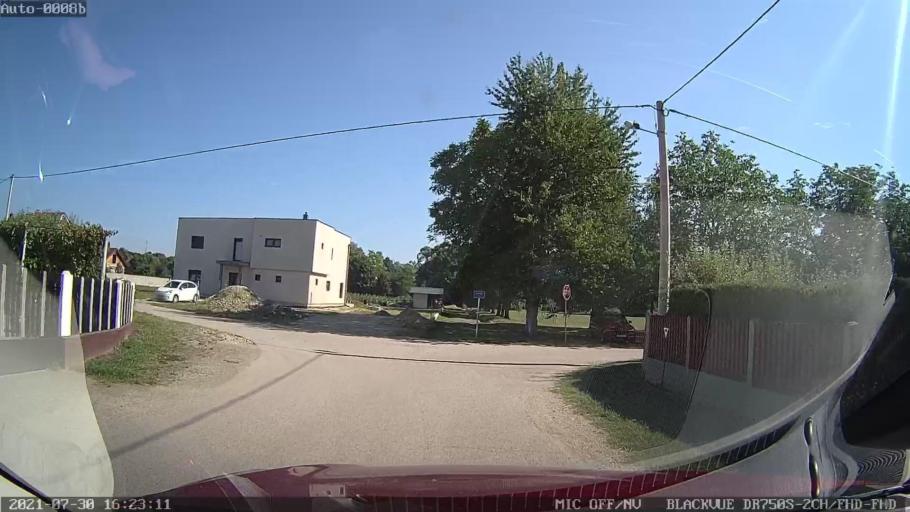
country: HR
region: Medimurska
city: Kursanec
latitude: 46.2874
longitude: 16.4026
